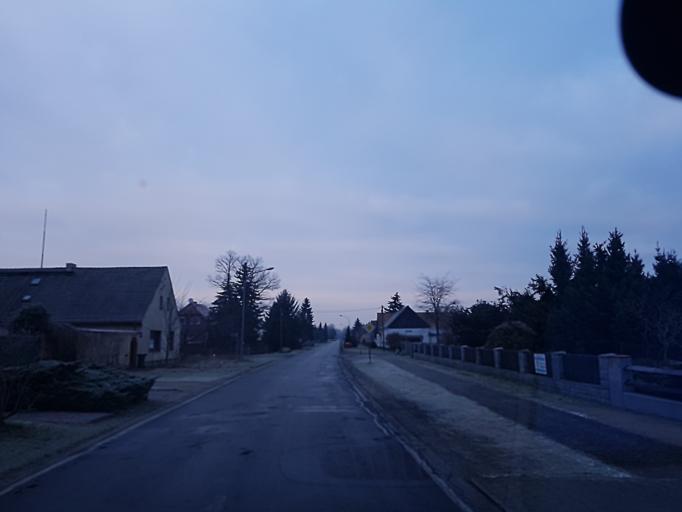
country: DE
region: Brandenburg
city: Finsterwalde
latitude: 51.6580
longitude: 13.7119
